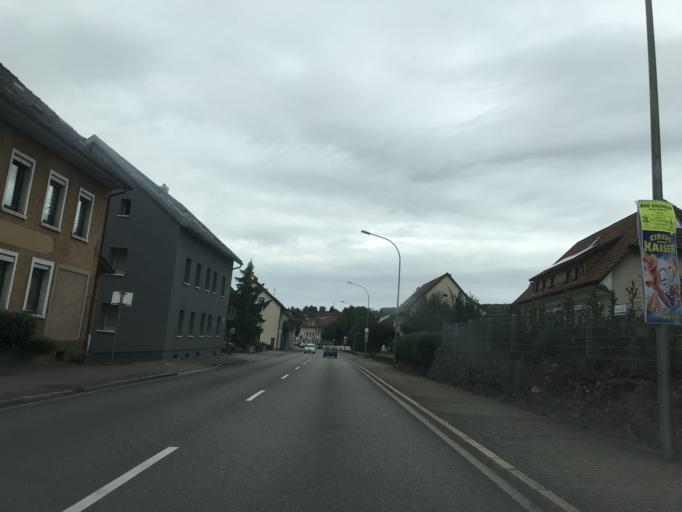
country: DE
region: Baden-Wuerttemberg
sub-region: Freiburg Region
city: Bad Sackingen
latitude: 47.5612
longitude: 7.9675
